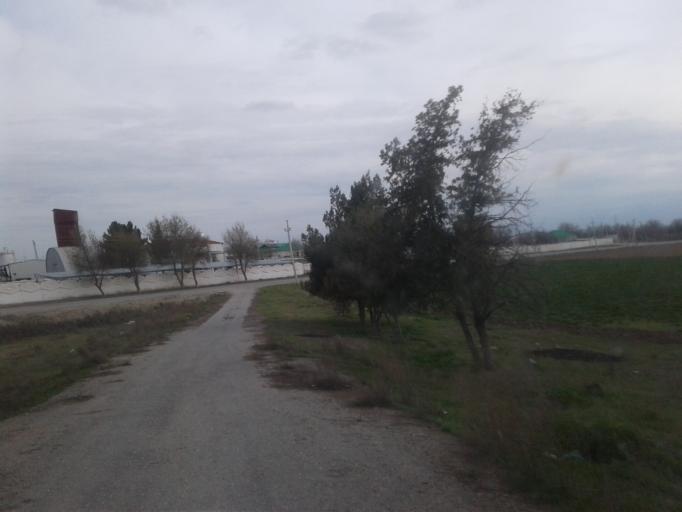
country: TM
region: Ahal
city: Abadan
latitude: 38.1237
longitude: 58.3451
